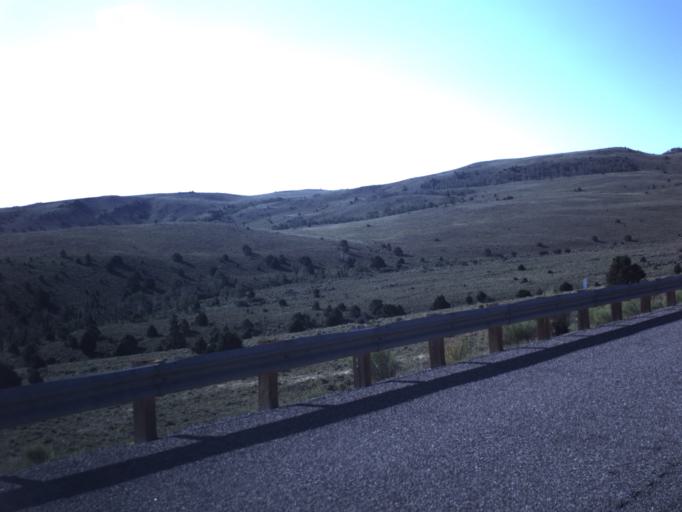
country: US
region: Utah
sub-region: Wayne County
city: Loa
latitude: 38.6056
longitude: -111.4623
